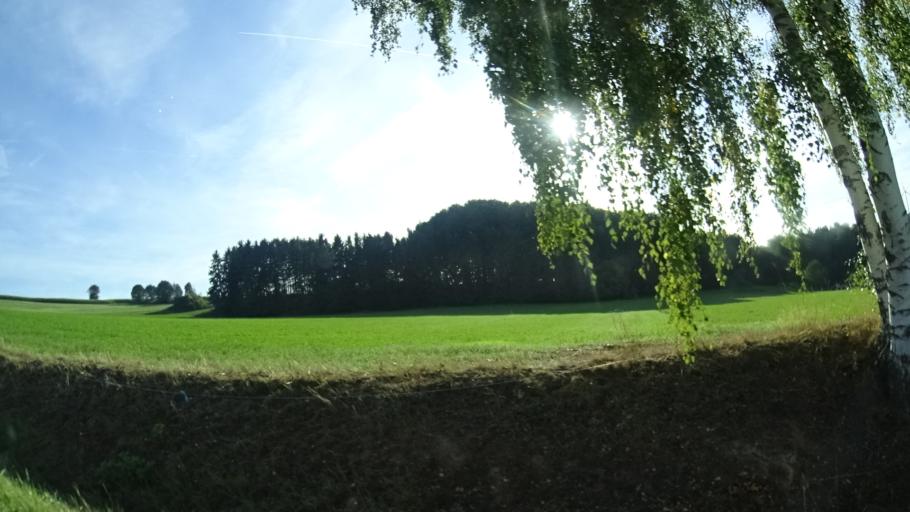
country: DE
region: Hesse
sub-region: Regierungsbezirk Kassel
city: Flieden
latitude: 50.4211
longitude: 9.5125
